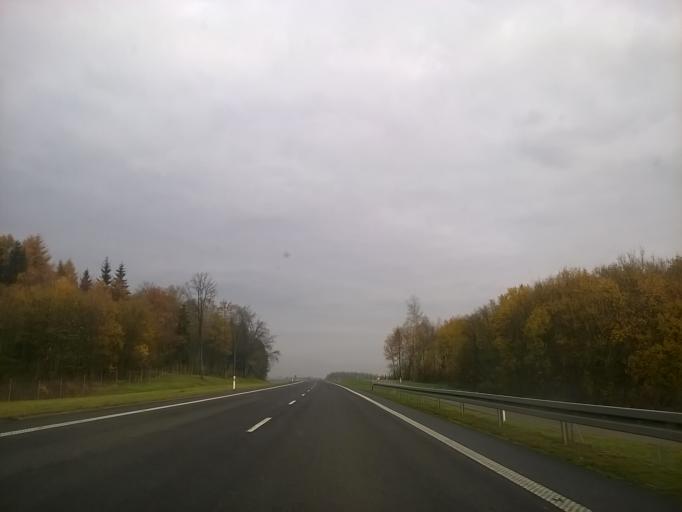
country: PL
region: Warmian-Masurian Voivodeship
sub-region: Powiat elblaski
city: Gronowo Gorne
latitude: 54.1562
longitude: 19.5076
